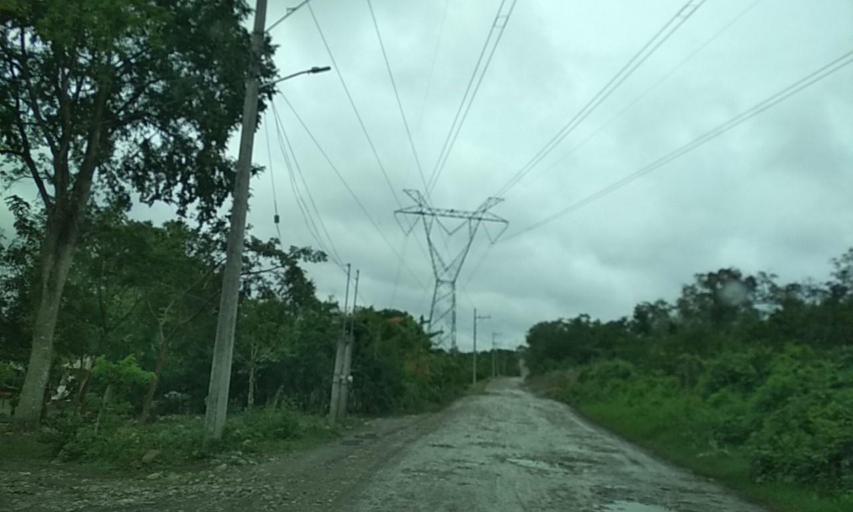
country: MX
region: Puebla
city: Espinal
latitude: 20.3115
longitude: -97.4149
